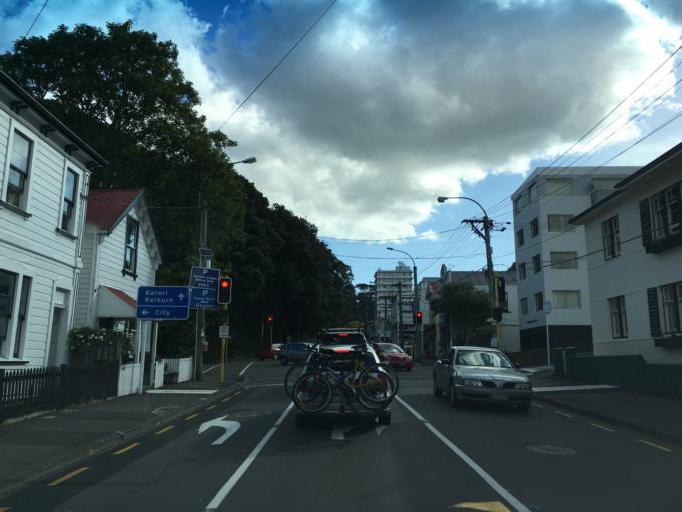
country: NZ
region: Wellington
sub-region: Wellington City
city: Kelburn
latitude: -41.2785
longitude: 174.7697
